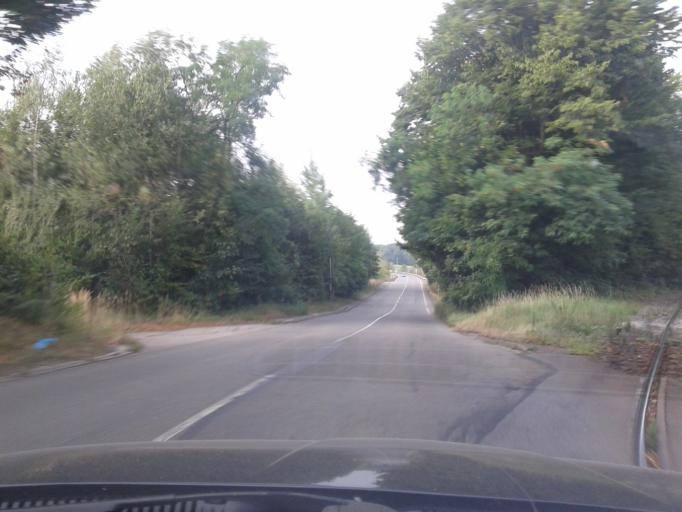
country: CZ
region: Moravskoslezsky
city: Orlova
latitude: 49.8427
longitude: 18.4485
